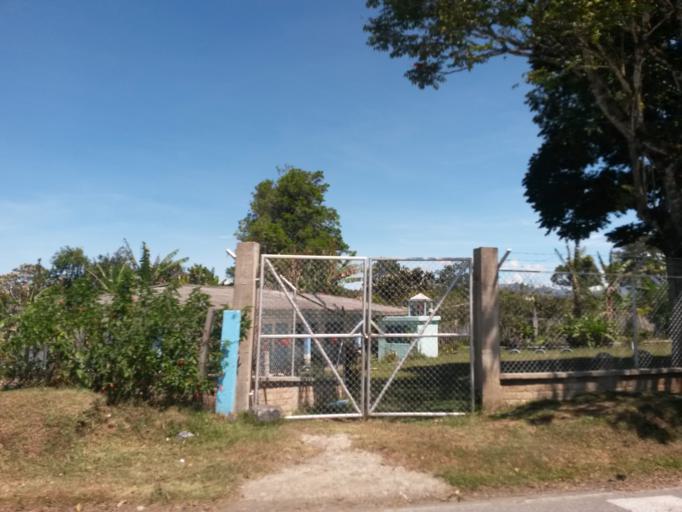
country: CO
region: Cauca
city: Lopez
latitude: 2.4463
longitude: -76.7926
